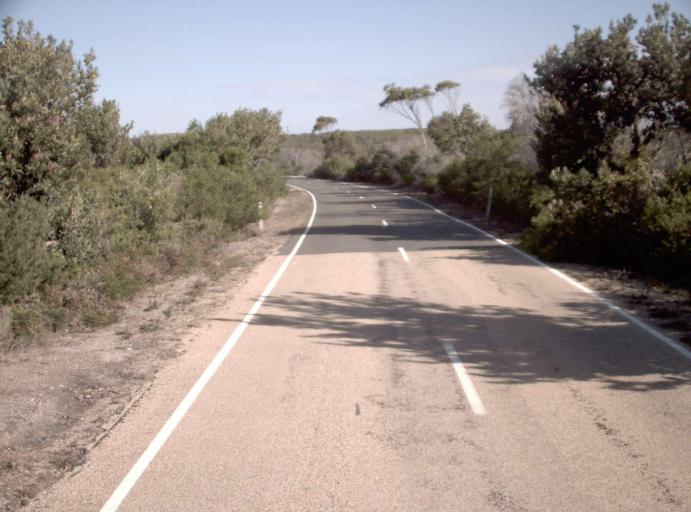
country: AU
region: Victoria
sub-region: East Gippsland
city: Lakes Entrance
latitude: -37.8005
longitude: 148.7221
